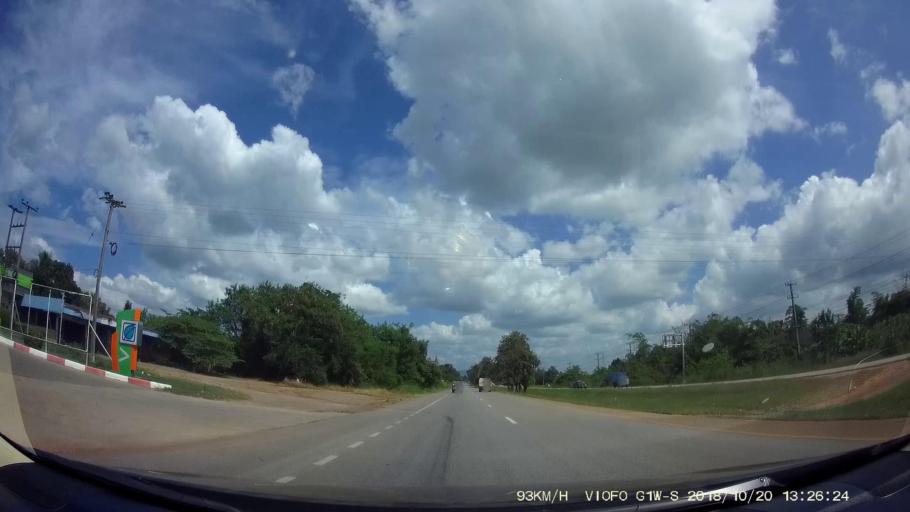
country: TH
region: Chaiyaphum
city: Khon San
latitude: 16.5938
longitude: 101.9457
